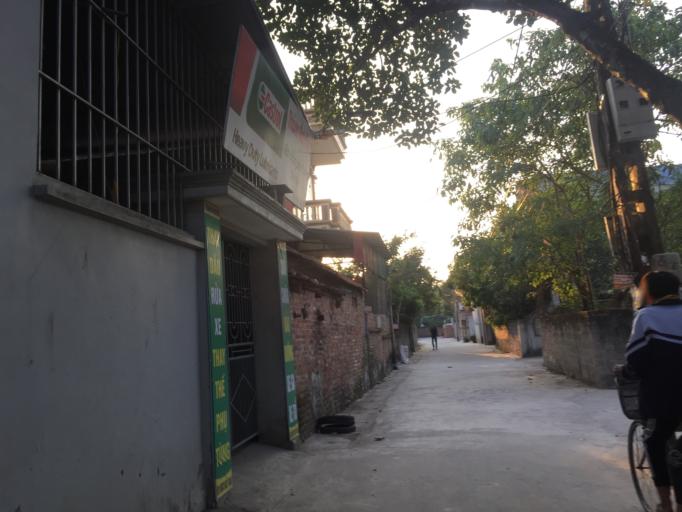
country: VN
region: Ha Noi
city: Chuc Son
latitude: 20.9049
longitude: 105.7236
